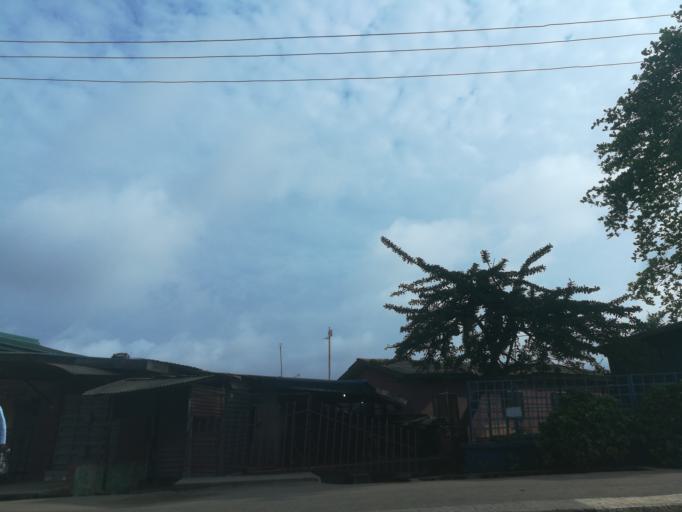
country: NG
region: Lagos
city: Agege
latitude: 6.6263
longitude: 3.3115
